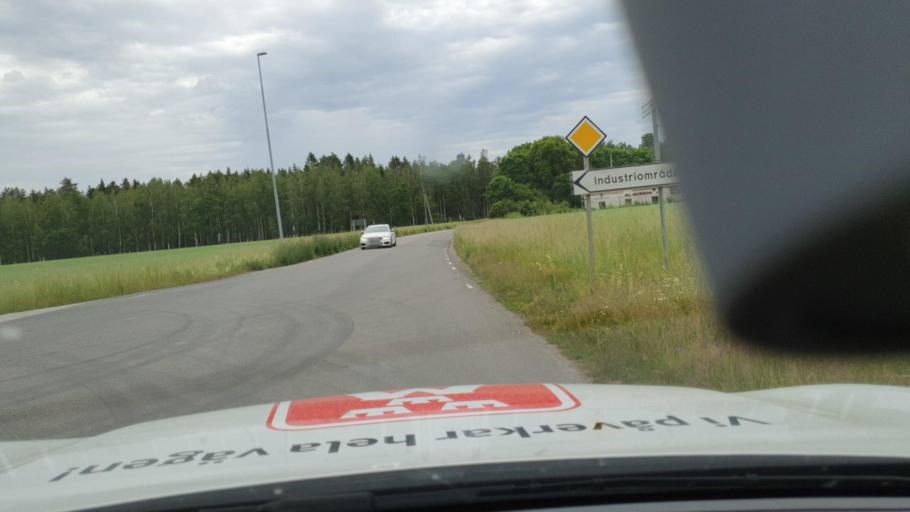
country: SE
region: Vaestra Goetaland
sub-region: Hjo Kommun
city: Hjo
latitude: 58.3166
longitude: 14.3050
